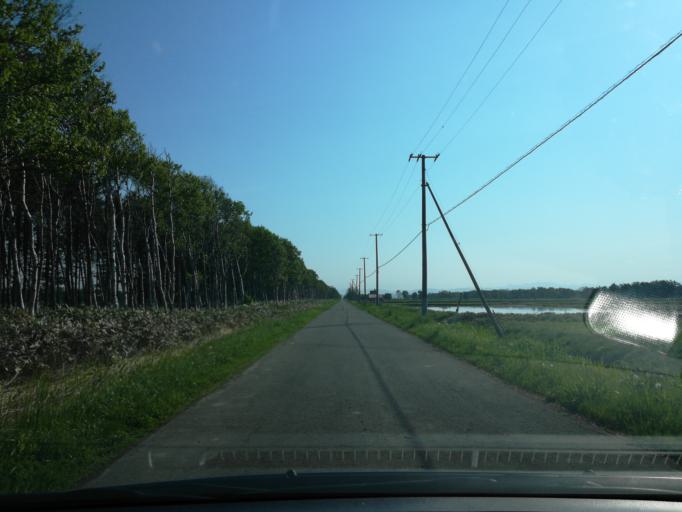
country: JP
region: Hokkaido
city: Ebetsu
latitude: 43.1130
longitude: 141.6412
